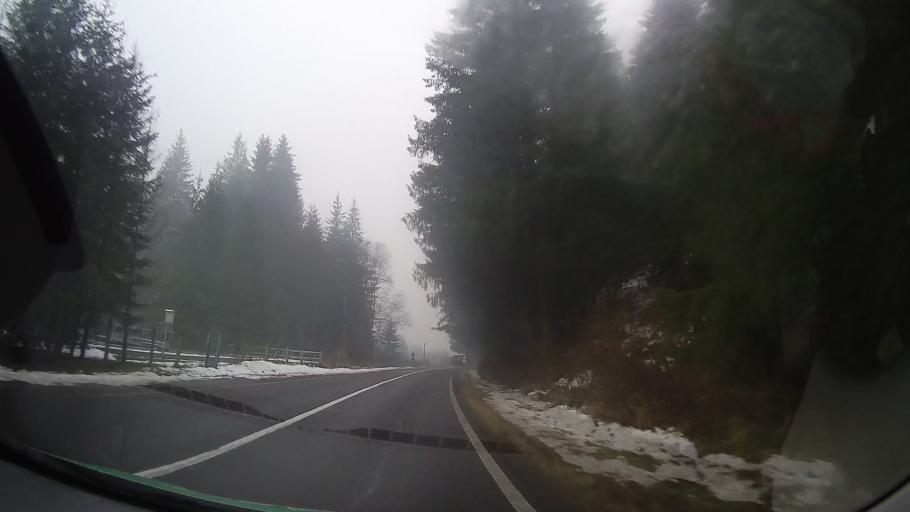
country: RO
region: Harghita
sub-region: Municipiul Gheorgheni
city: Gheorgheni
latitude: 46.7488
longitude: 25.6838
